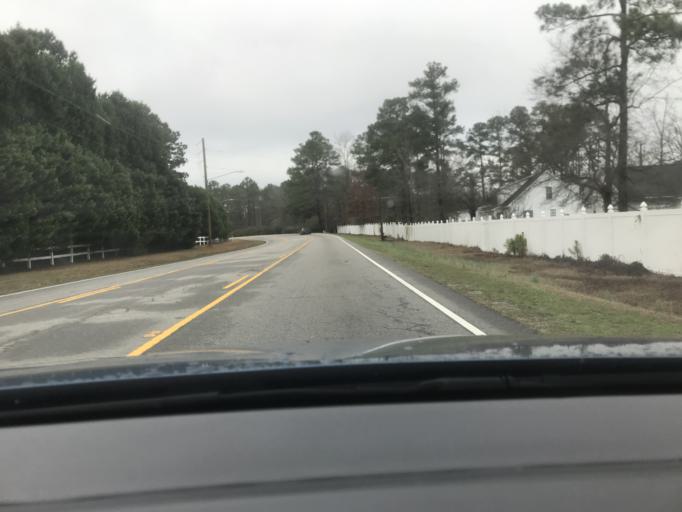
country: US
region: North Carolina
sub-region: Hoke County
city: Rockfish
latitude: 35.0439
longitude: -79.0078
